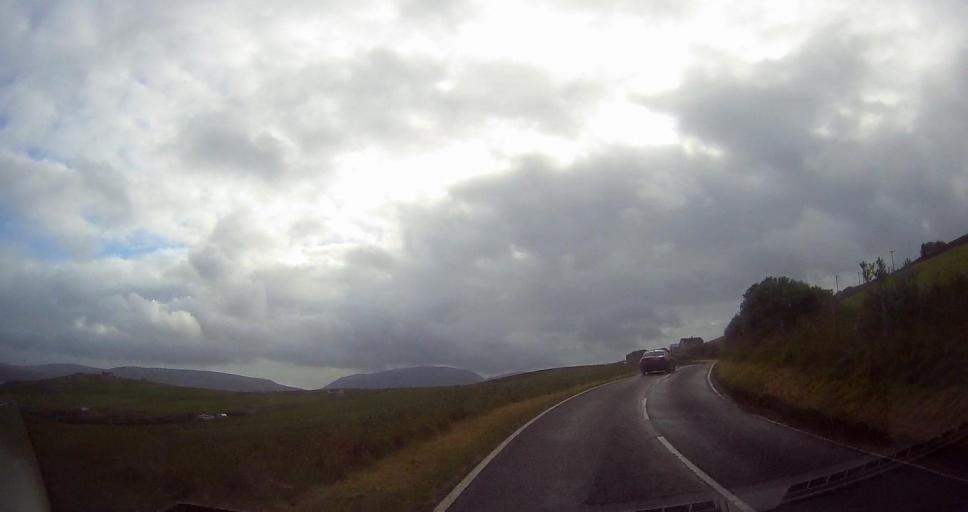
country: GB
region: Scotland
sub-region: Orkney Islands
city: Stromness
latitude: 58.9208
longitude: -3.1896
